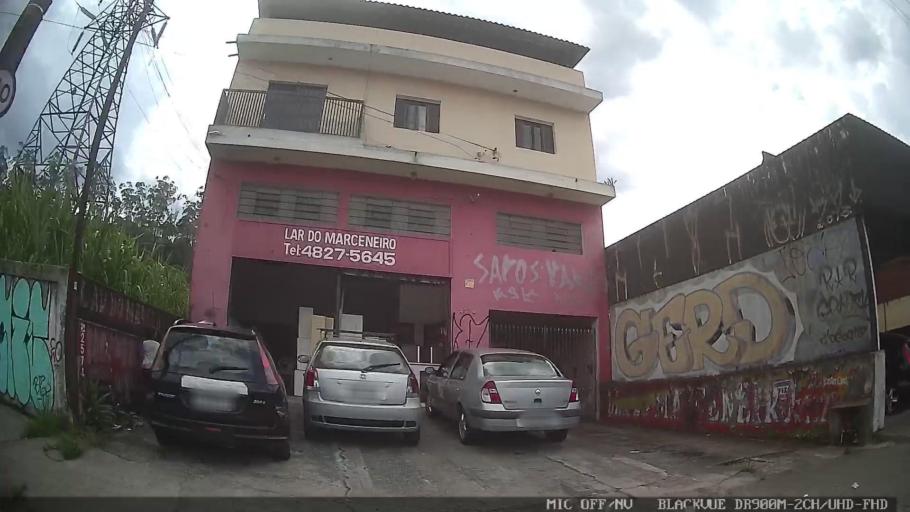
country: BR
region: Sao Paulo
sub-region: Ribeirao Pires
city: Ribeirao Pires
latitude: -23.6977
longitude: -46.3963
